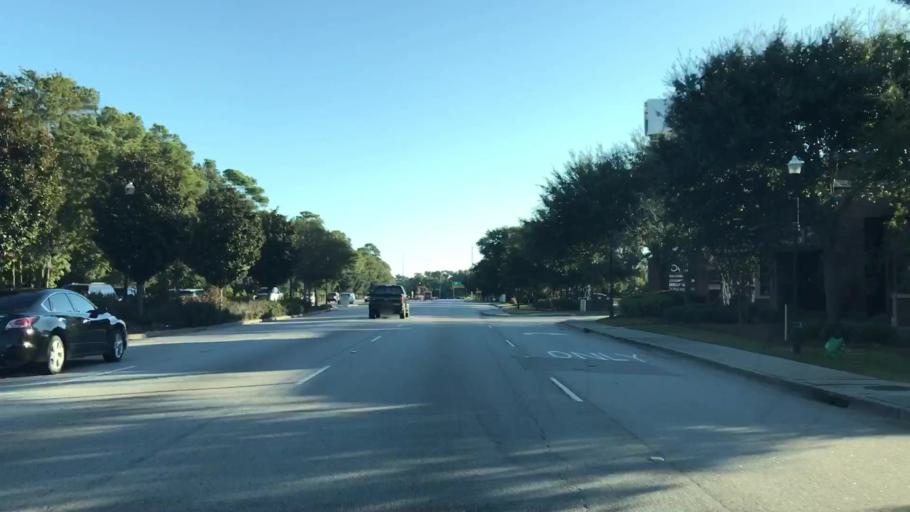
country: US
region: South Carolina
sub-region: Charleston County
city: Mount Pleasant
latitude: 32.8313
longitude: -79.8303
